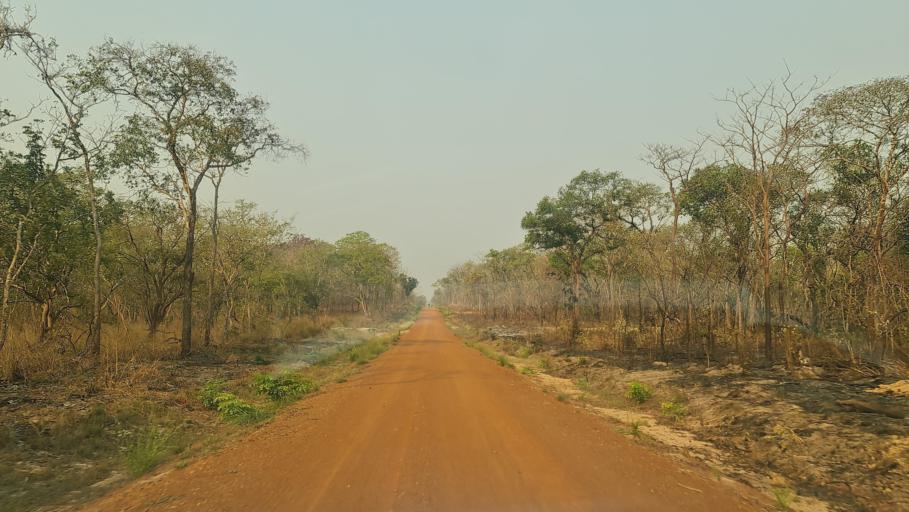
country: MZ
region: Zambezia
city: Quelimane
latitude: -17.1222
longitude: 37.1495
